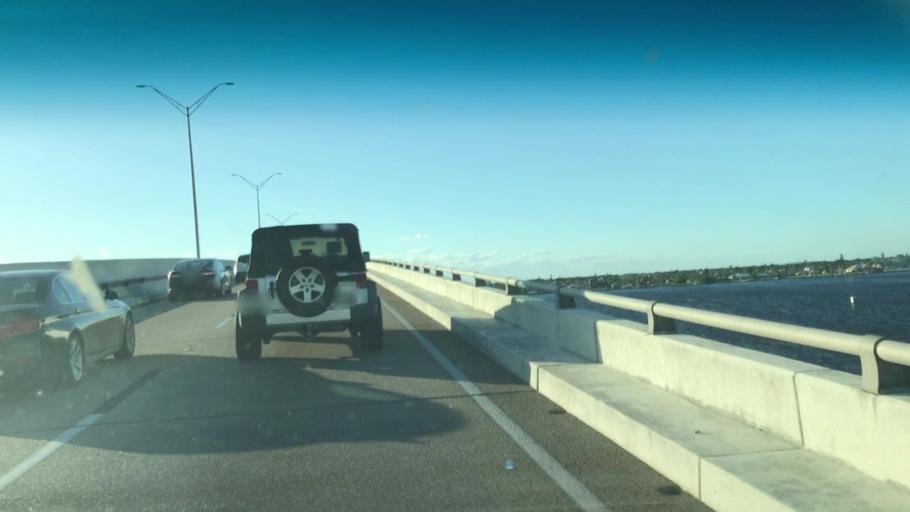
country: US
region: Florida
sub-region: Lee County
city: McGregor
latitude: 26.5606
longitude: -81.9274
